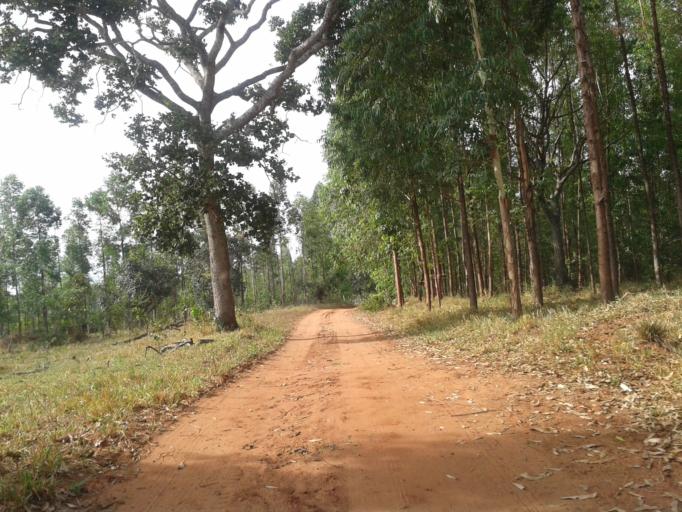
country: BR
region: Minas Gerais
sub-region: Campina Verde
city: Campina Verde
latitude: -19.4508
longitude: -49.6024
